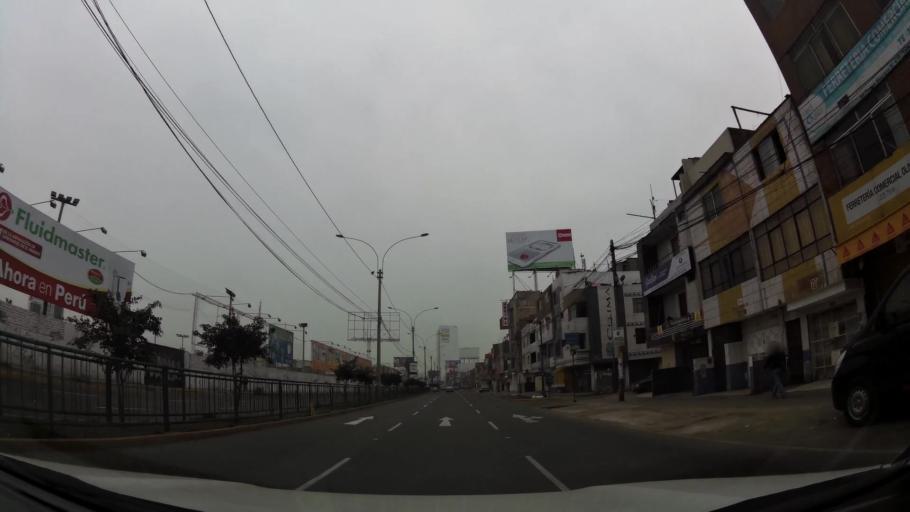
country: PE
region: Lima
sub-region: Lima
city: Surco
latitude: -12.1106
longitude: -77.0135
